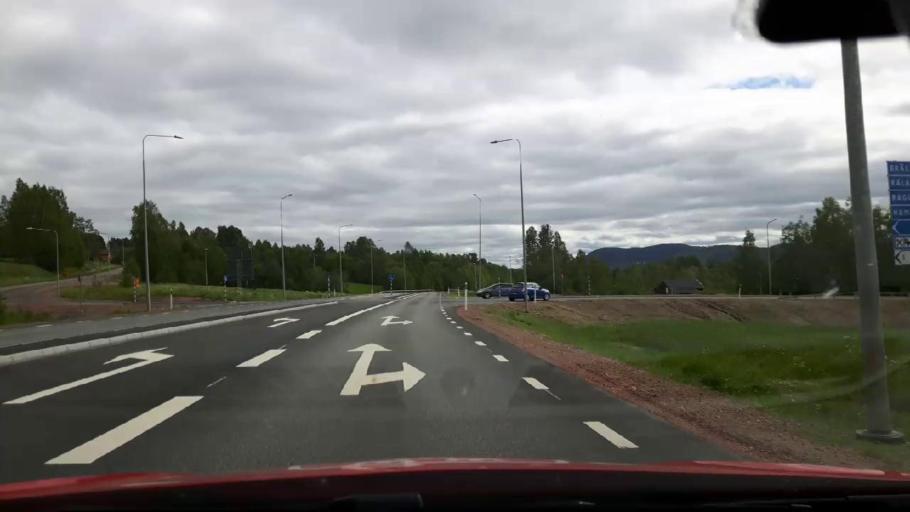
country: SE
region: Jaemtland
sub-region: Ragunda Kommun
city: Hammarstrand
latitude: 63.1185
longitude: 16.3641
